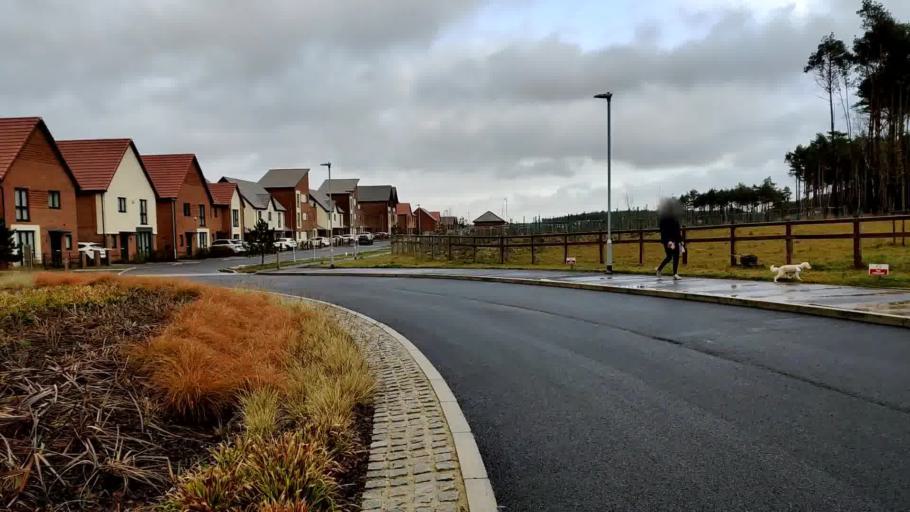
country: GB
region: England
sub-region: Bracknell Forest
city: Crowthorne
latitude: 51.3765
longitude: -0.7895
